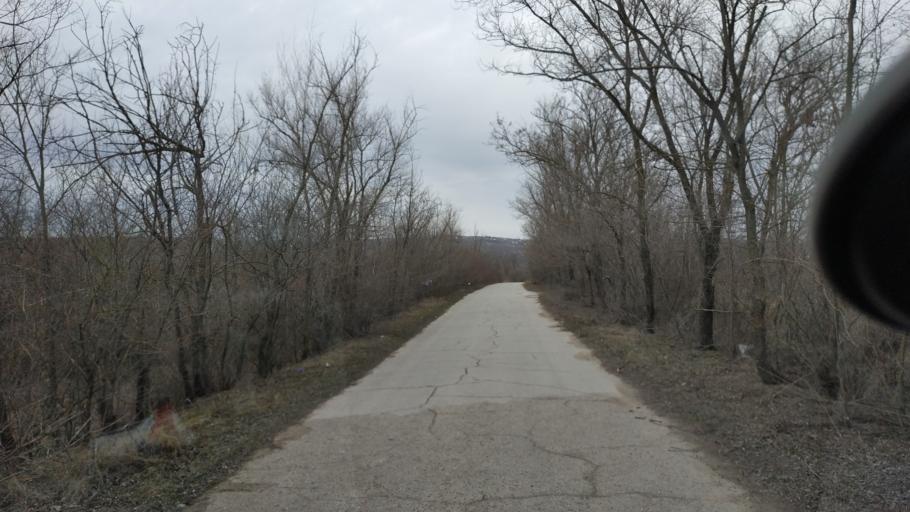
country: MD
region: Telenesti
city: Cocieri
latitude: 47.3289
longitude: 29.0912
